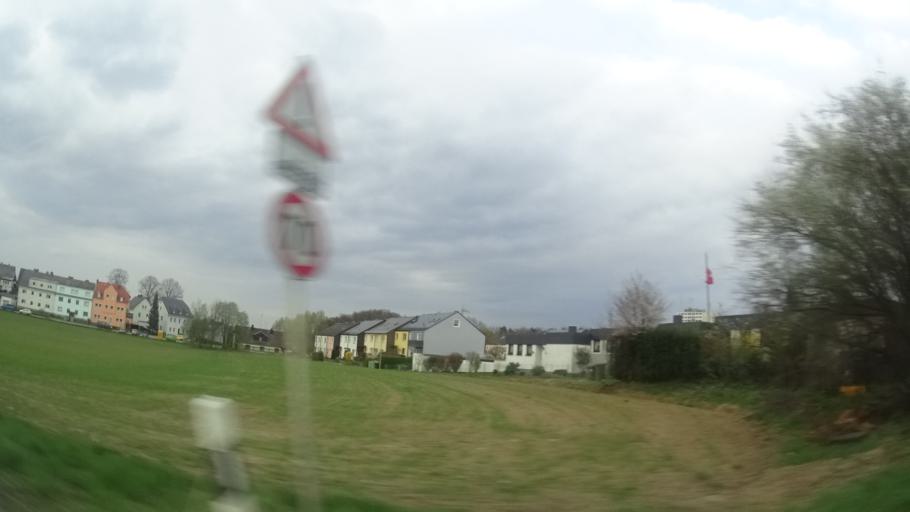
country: DE
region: Bavaria
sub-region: Upper Franconia
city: Hof
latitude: 50.3282
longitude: 11.8916
